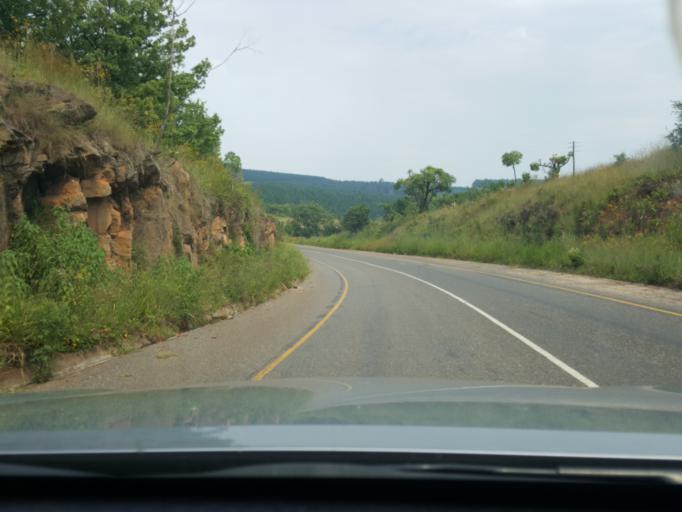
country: ZA
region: Mpumalanga
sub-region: Ehlanzeni District
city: White River
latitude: -25.2436
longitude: 30.9534
